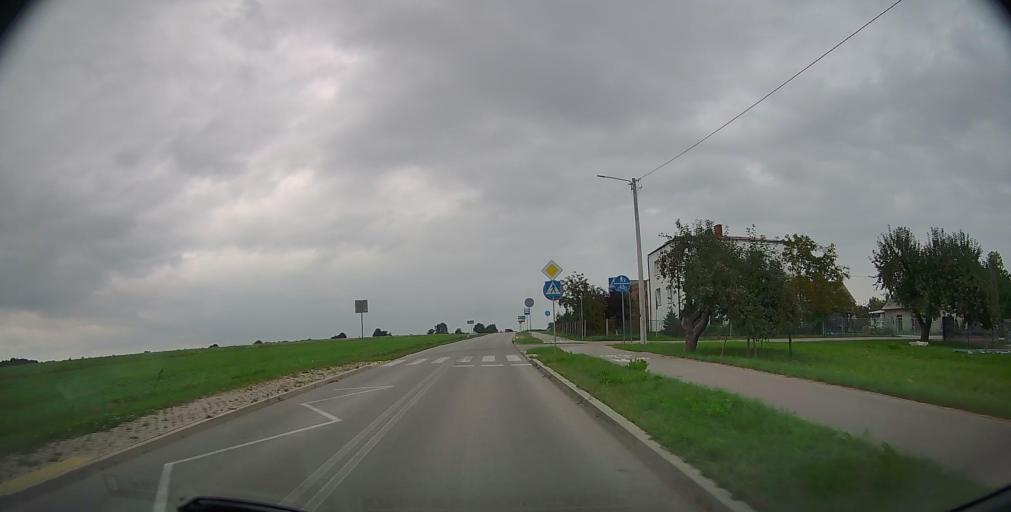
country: PL
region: Masovian Voivodeship
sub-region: Powiat radomski
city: Zakrzew
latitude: 51.4375
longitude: 21.0522
